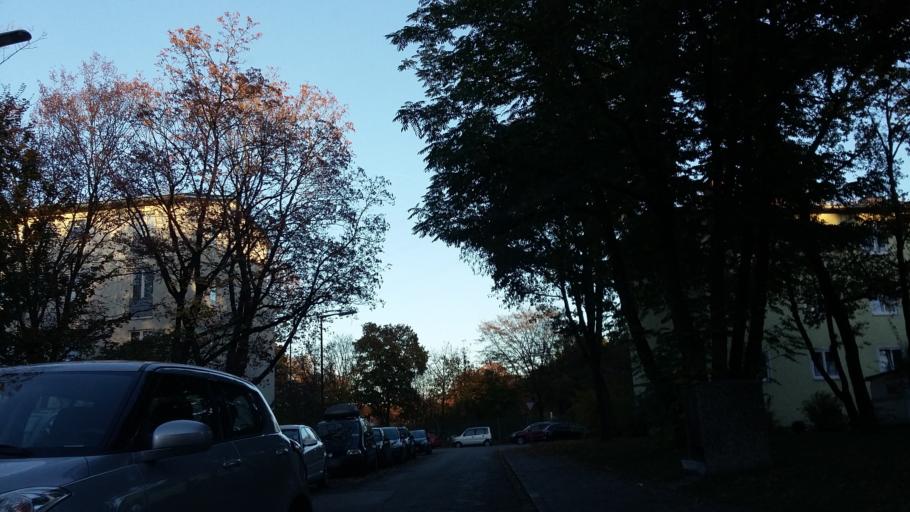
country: DE
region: Bavaria
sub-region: Upper Bavaria
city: Pasing
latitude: 48.1265
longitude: 11.4922
